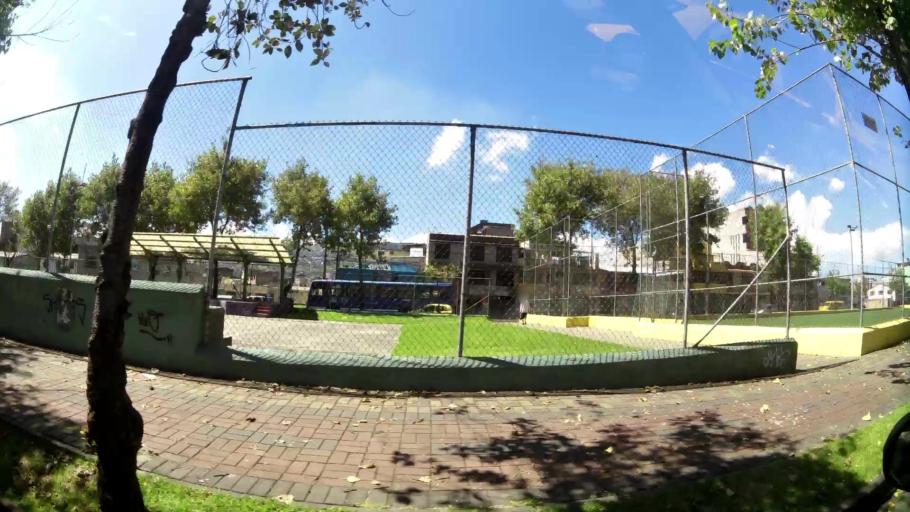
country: EC
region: Pichincha
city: Quito
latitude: -0.2566
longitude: -78.5328
